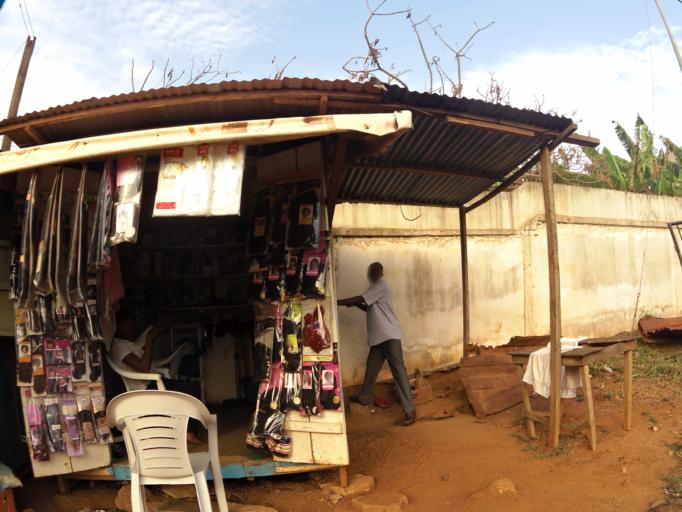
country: GH
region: Greater Accra
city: Dome
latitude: 5.6434
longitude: -0.2141
